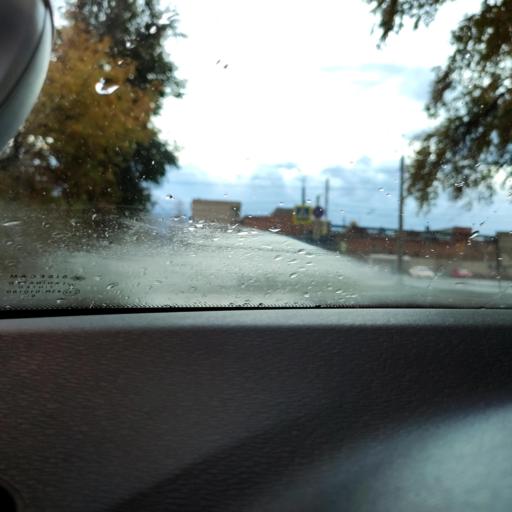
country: RU
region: Samara
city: Smyshlyayevka
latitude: 53.2026
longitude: 50.2835
